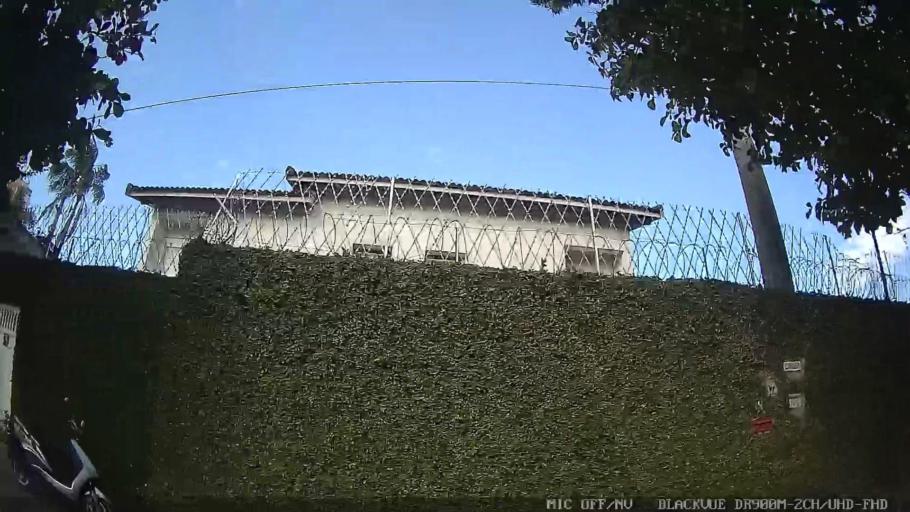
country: BR
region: Sao Paulo
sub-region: Guaruja
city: Guaruja
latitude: -23.9799
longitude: -46.2096
